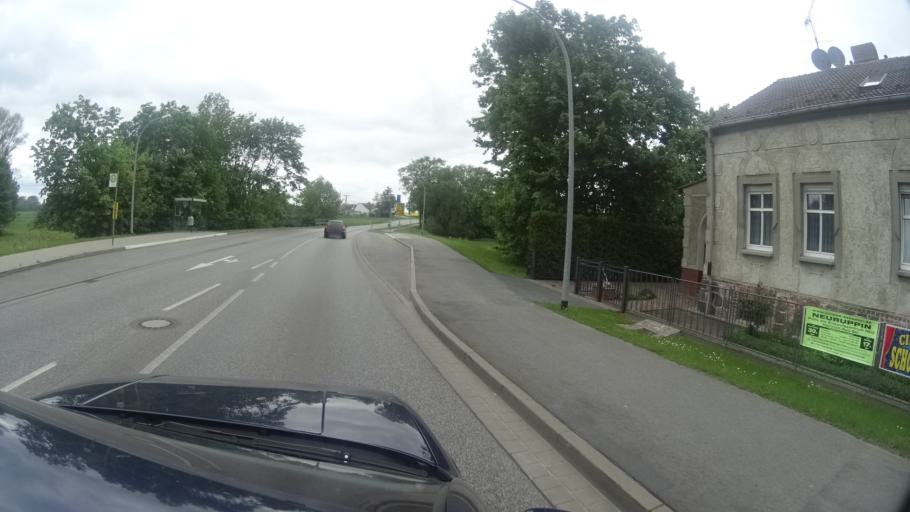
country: DE
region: Brandenburg
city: Fehrbellin
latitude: 52.8376
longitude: 12.7798
